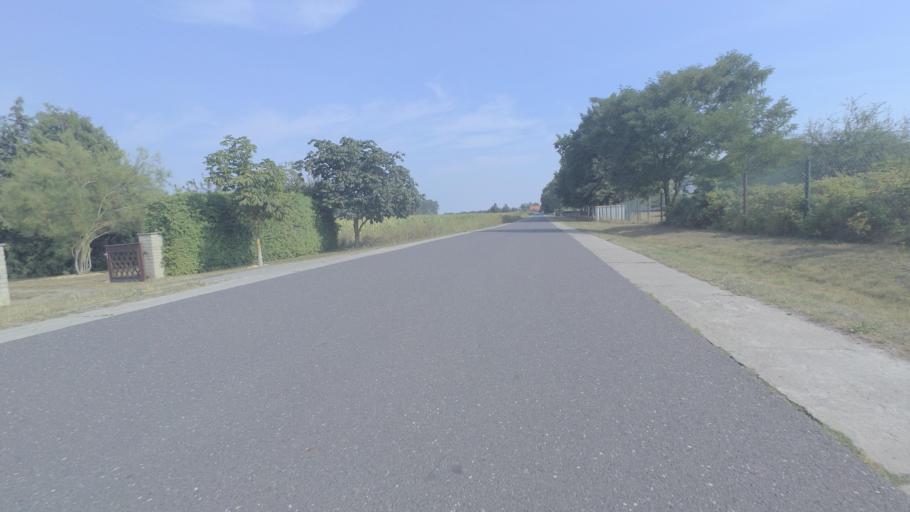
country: DE
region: Mecklenburg-Vorpommern
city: Wendorf
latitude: 54.2513
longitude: 13.0732
